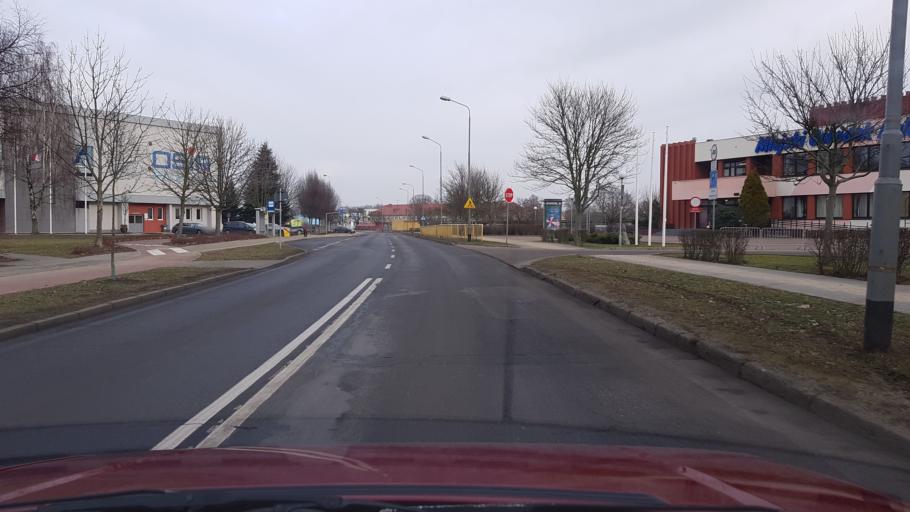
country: PL
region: West Pomeranian Voivodeship
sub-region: Powiat policki
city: Police
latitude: 53.5474
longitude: 14.5640
